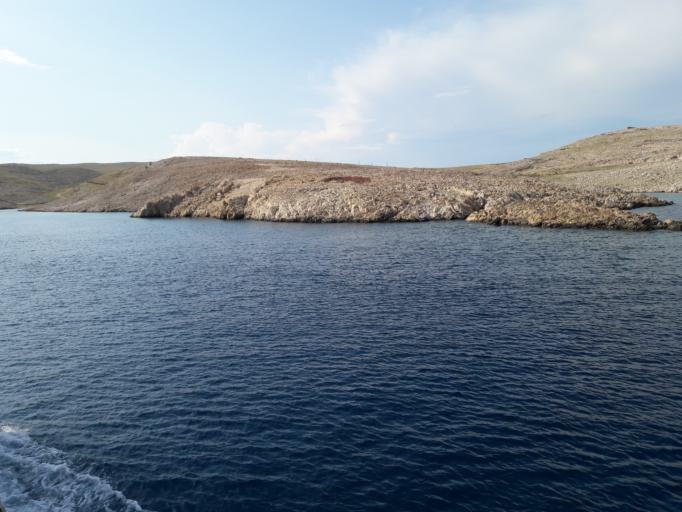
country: HR
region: Primorsko-Goranska
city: Banjol
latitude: 44.7054
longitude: 14.8644
